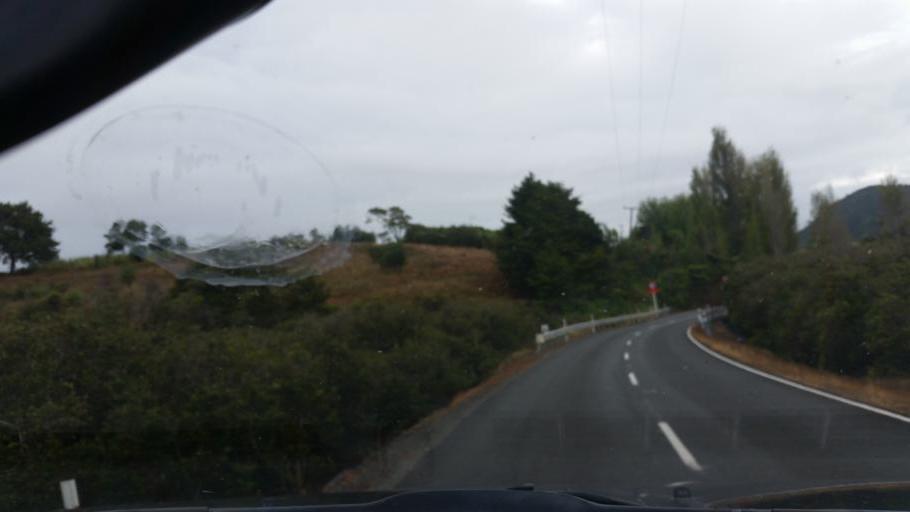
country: NZ
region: Auckland
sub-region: Auckland
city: Wellsford
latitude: -36.1202
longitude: 174.3643
